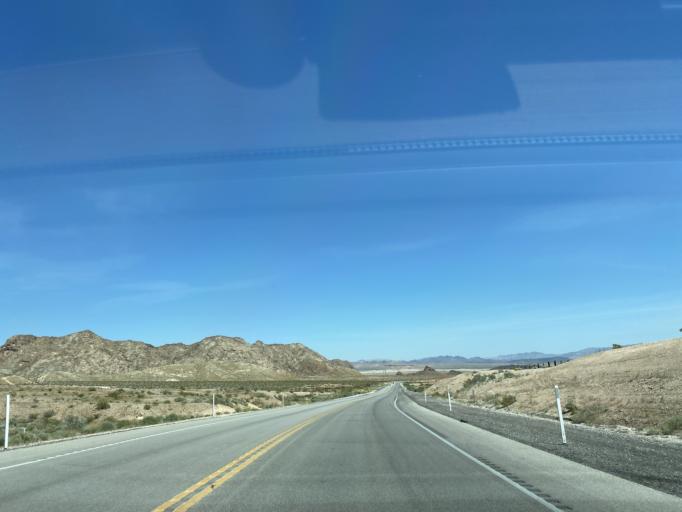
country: US
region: Nevada
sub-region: Clark County
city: Nellis Air Force Base
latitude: 36.2067
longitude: -114.9593
